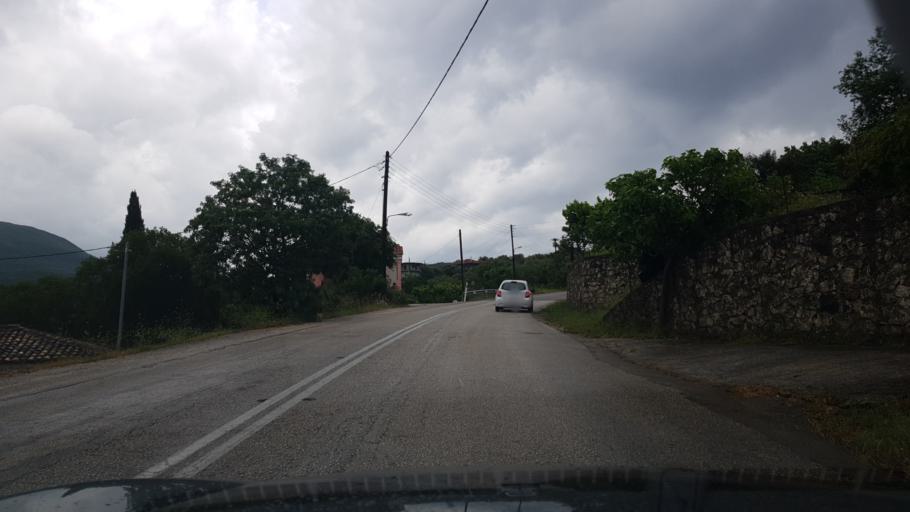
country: GR
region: Ionian Islands
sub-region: Lefkada
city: Nidri
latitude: 38.6321
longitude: 20.6517
